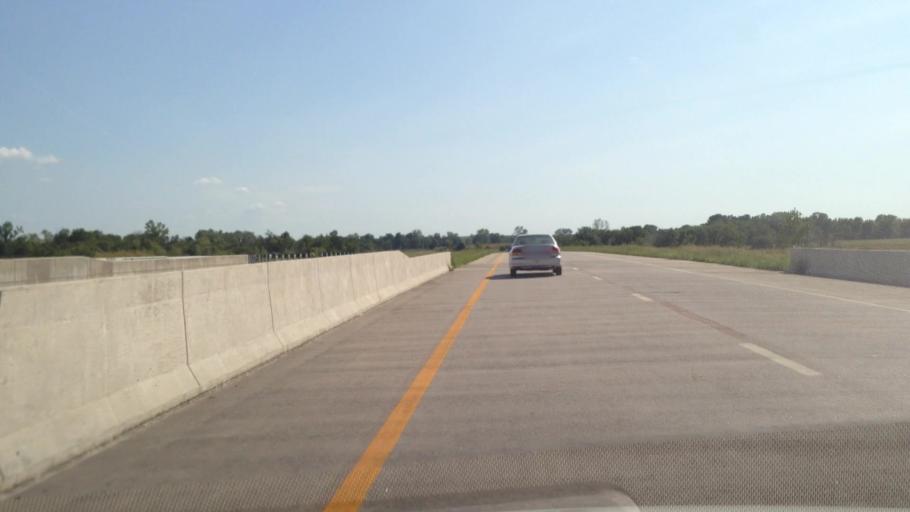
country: US
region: Kansas
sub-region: Bourbon County
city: Fort Scott
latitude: 37.9682
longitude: -94.7062
